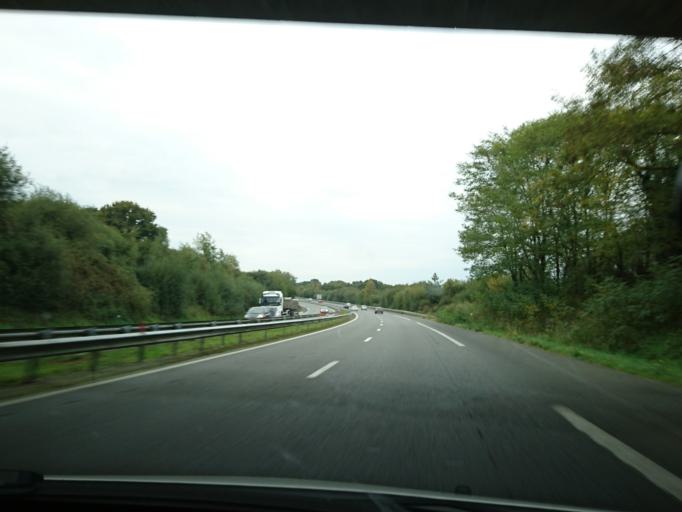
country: FR
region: Brittany
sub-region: Departement du Morbihan
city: Nivillac
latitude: 47.5292
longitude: -2.2863
